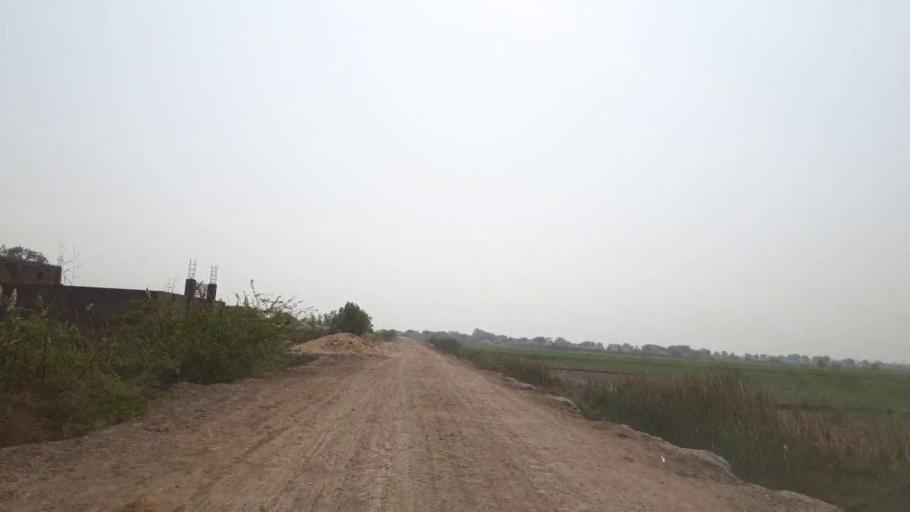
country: PK
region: Sindh
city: Mirpur Khas
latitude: 25.5393
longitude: 69.0620
